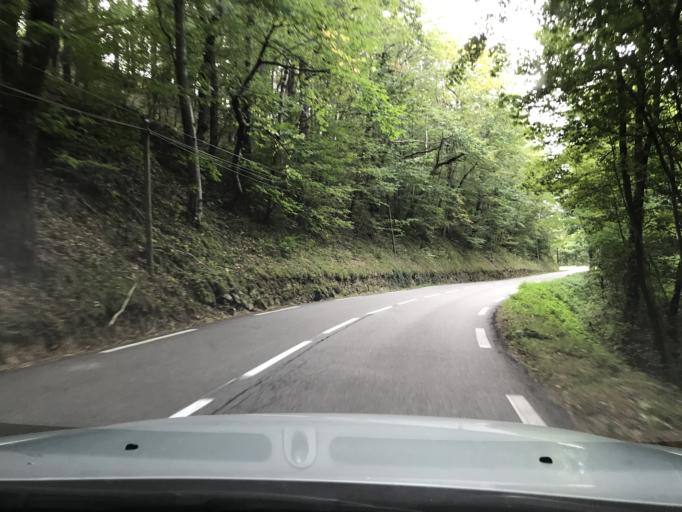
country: FR
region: Rhone-Alpes
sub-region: Departement de l'Ardeche
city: Lamastre
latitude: 44.9832
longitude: 4.5940
